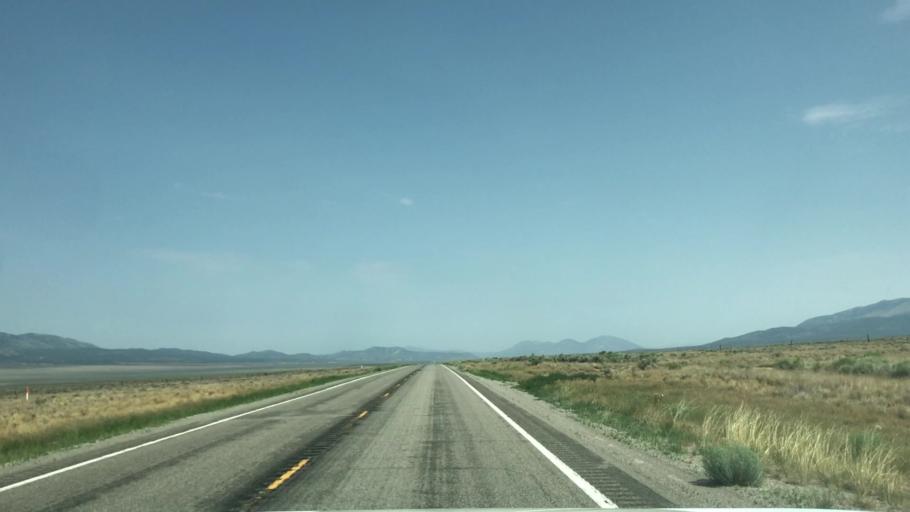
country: US
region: Nevada
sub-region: White Pine County
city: Ely
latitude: 39.0565
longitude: -114.7291
